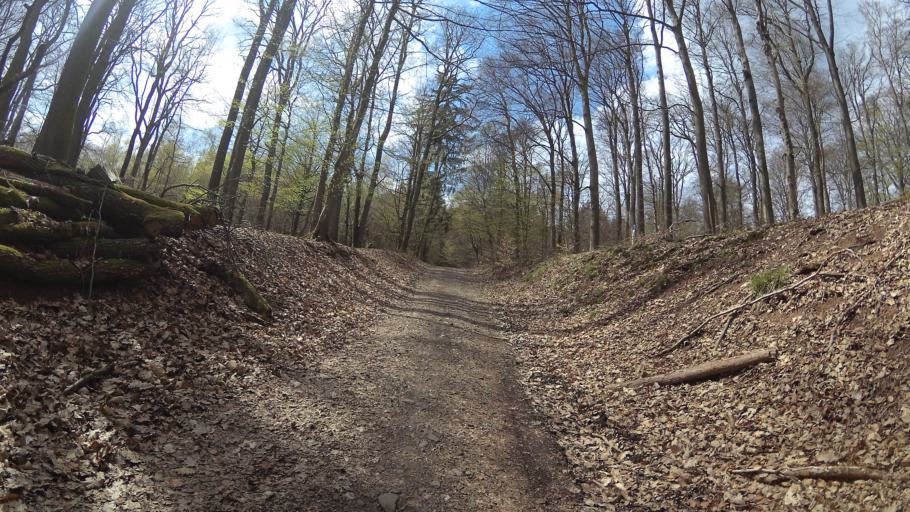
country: DE
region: Saarland
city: Marpingen
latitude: 49.4557
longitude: 7.0992
